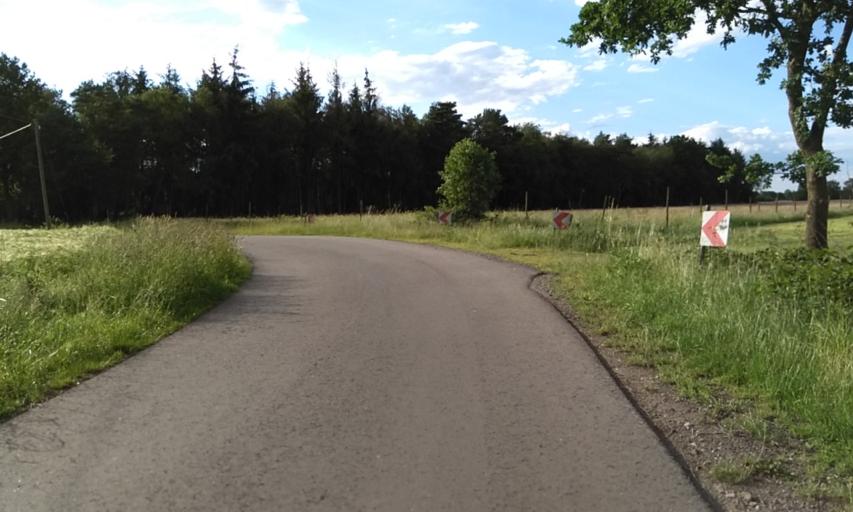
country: DE
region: Lower Saxony
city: Ahlerstedt
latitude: 53.3603
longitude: 9.4639
